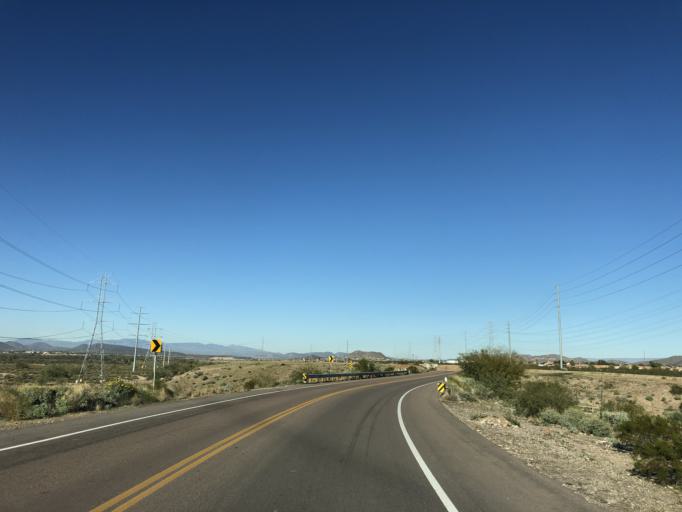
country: US
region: Arizona
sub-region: Maricopa County
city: Sun City West
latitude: 33.6781
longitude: -112.2998
